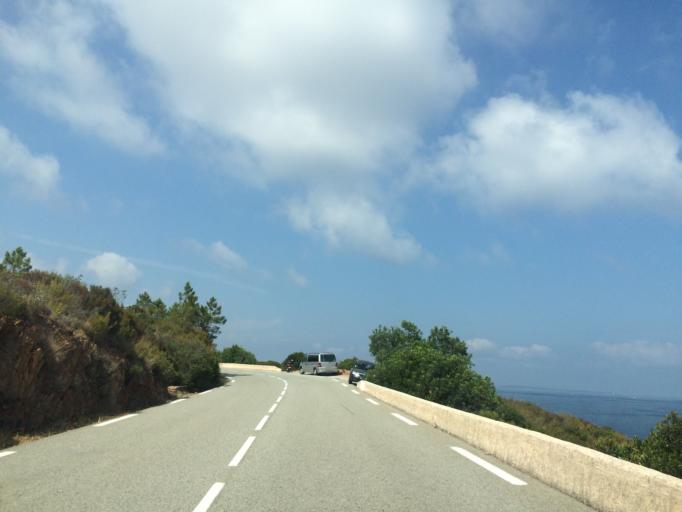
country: FR
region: Provence-Alpes-Cote d'Azur
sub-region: Departement des Alpes-Maritimes
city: Theoule-sur-Mer
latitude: 43.4543
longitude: 6.9208
